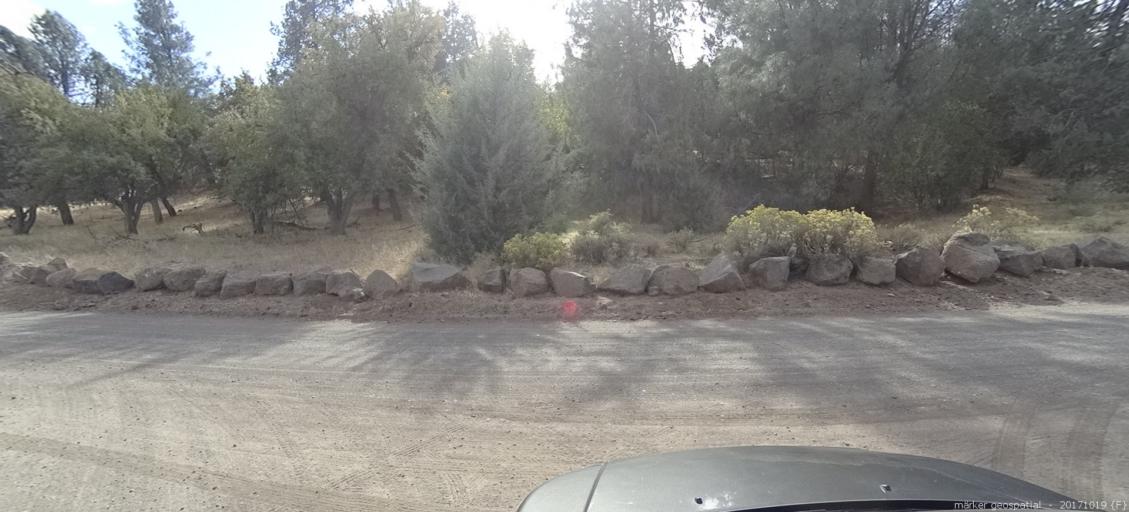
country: US
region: California
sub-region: Shasta County
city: Burney
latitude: 41.0065
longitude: -121.4458
